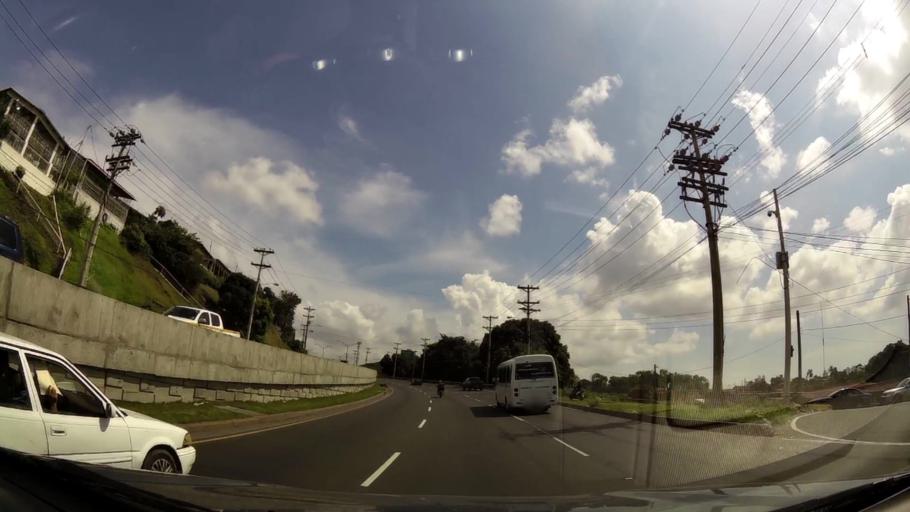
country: PA
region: Panama
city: San Miguelito
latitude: 9.0288
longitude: -79.4945
